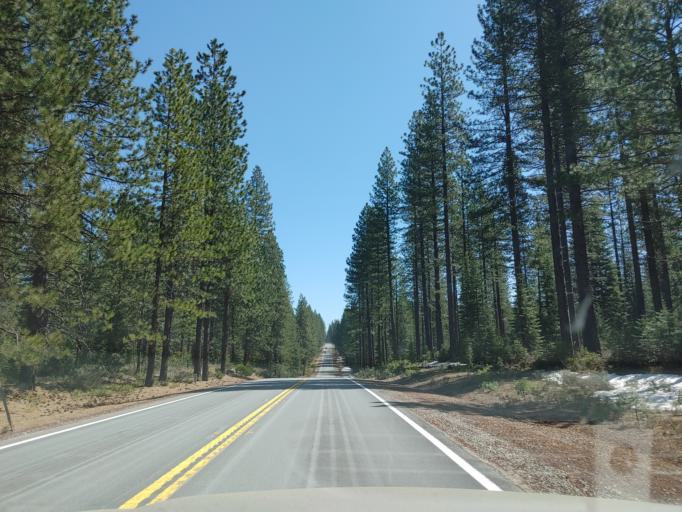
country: US
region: California
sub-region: Siskiyou County
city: McCloud
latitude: 41.2670
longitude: -121.8973
